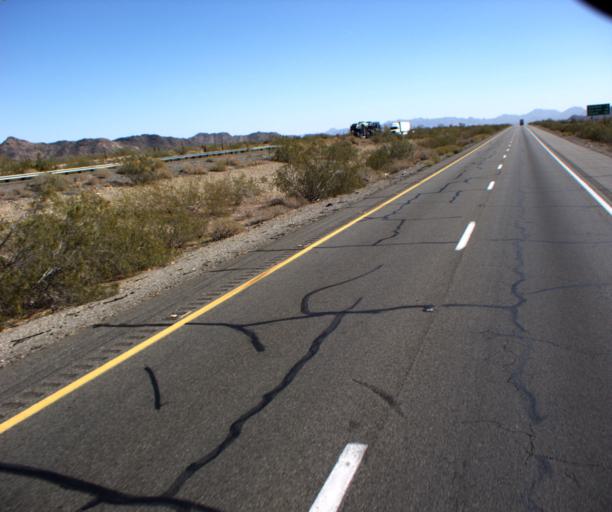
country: US
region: Arizona
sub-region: La Paz County
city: Quartzsite
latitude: 33.6478
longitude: -114.3233
